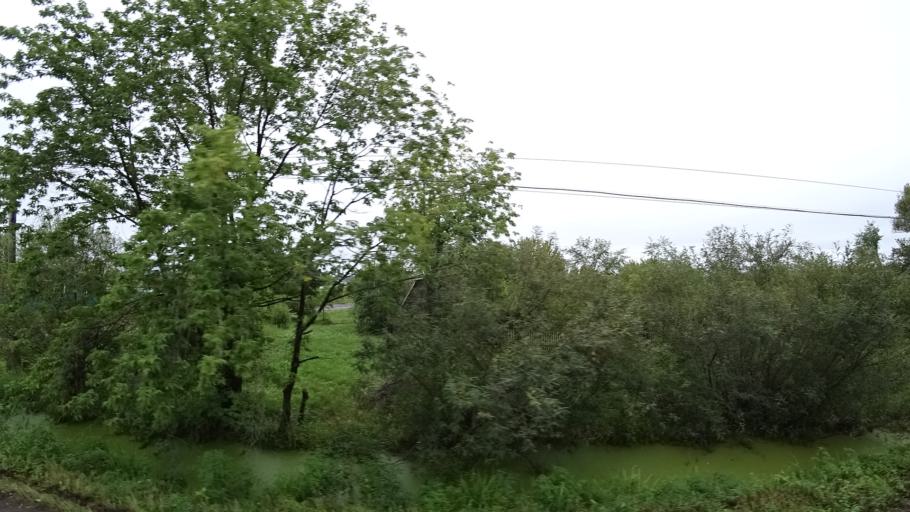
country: RU
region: Primorskiy
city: Monastyrishche
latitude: 44.2018
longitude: 132.4676
